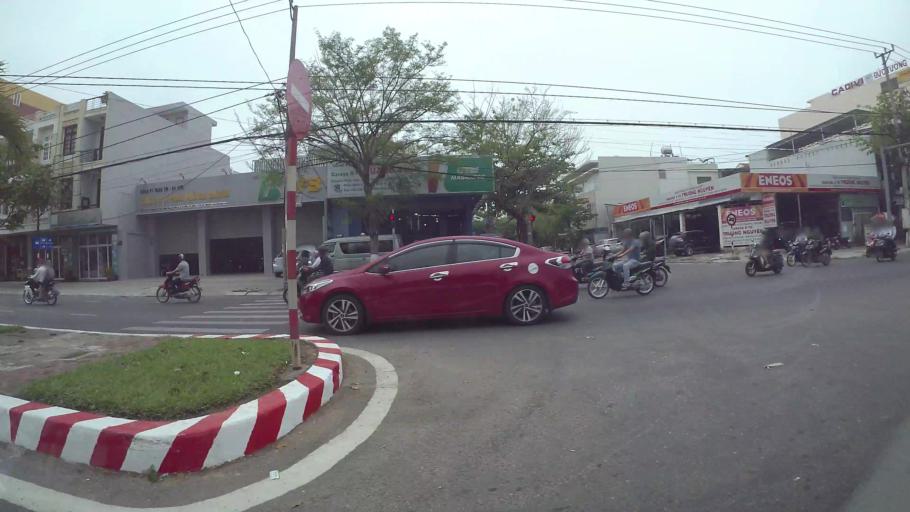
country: VN
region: Da Nang
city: Cam Le
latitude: 16.0338
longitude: 108.2093
